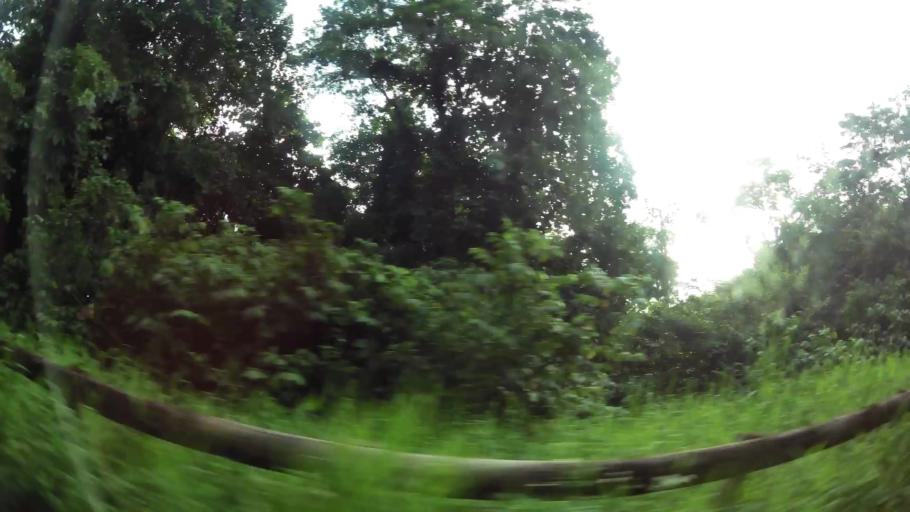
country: GP
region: Guadeloupe
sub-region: Guadeloupe
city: Bouillante
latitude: 16.1785
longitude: -61.7198
